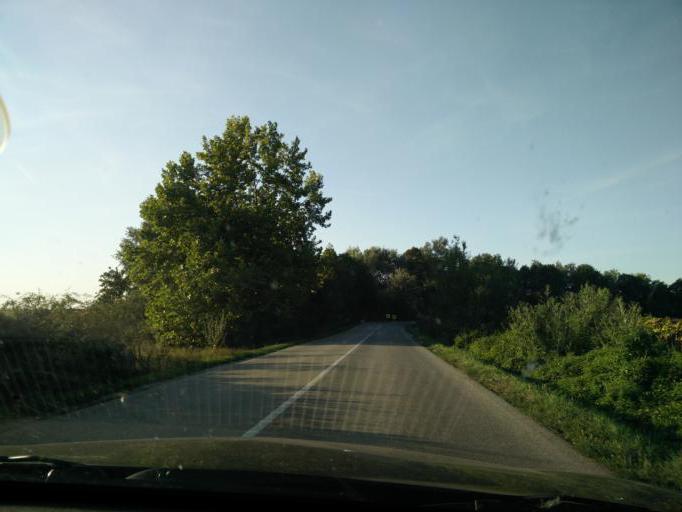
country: HU
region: Pest
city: Perbal
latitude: 47.6034
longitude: 18.7686
